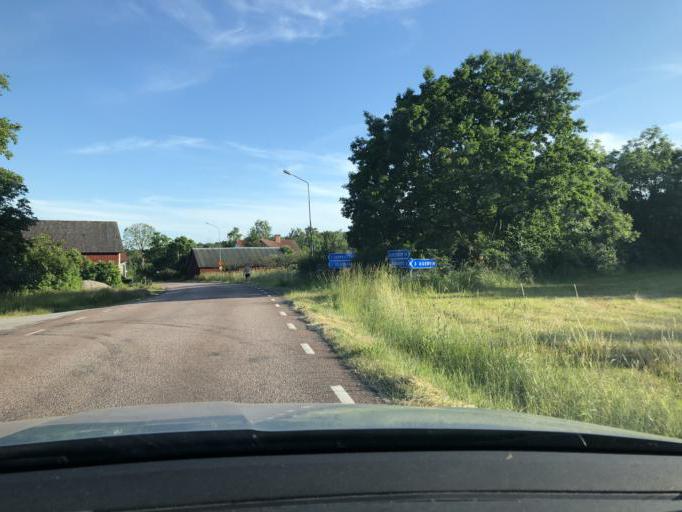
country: SE
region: Blekinge
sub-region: Solvesborgs Kommun
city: Soelvesborg
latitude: 56.1351
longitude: 14.6070
